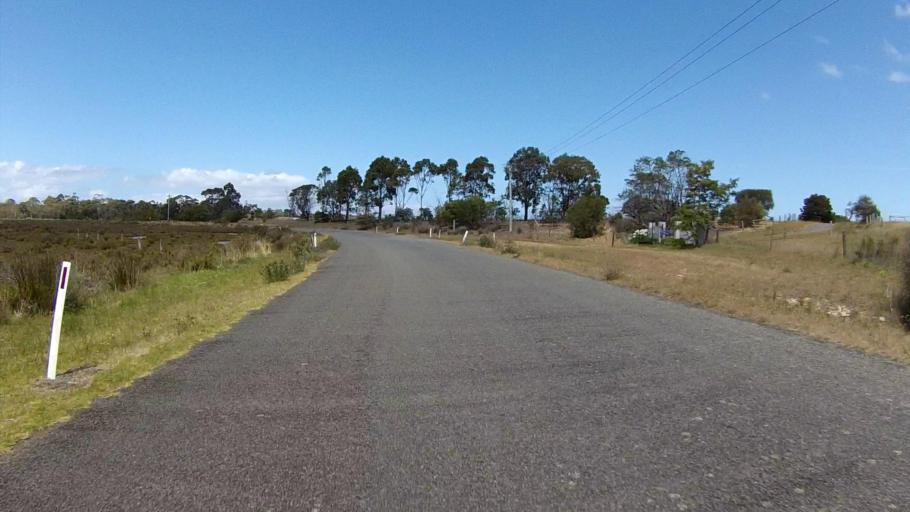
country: AU
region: Tasmania
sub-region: Clarence
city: Lauderdale
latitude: -42.9287
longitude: 147.4831
